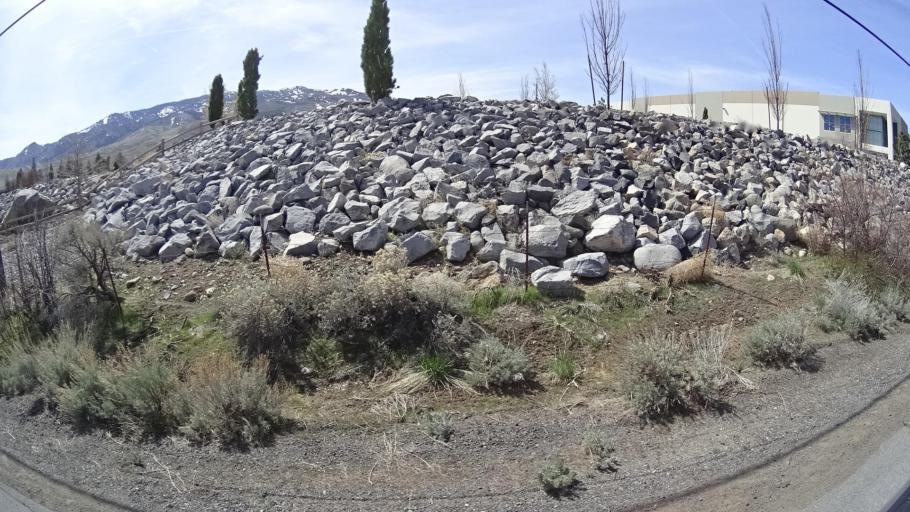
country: US
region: Nevada
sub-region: Washoe County
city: Verdi
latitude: 39.5182
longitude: -119.9654
